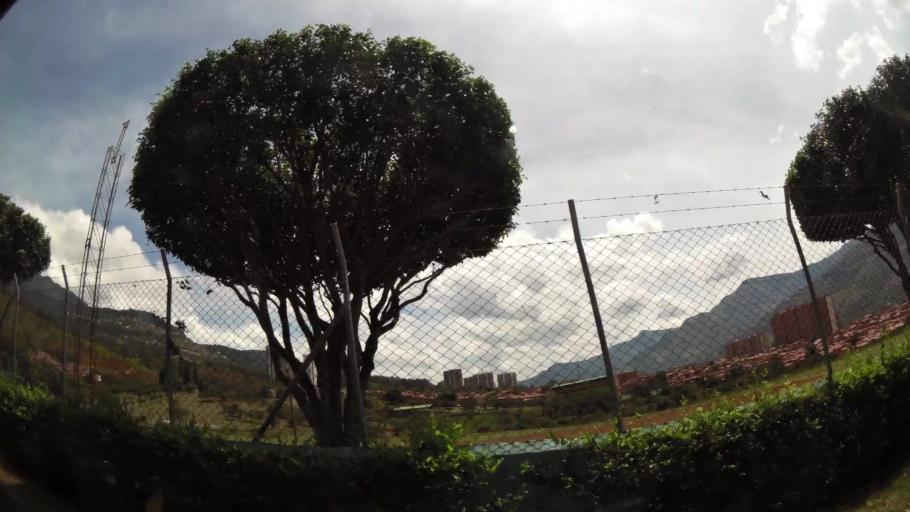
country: CO
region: Antioquia
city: Bello
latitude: 6.3440
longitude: -75.5445
